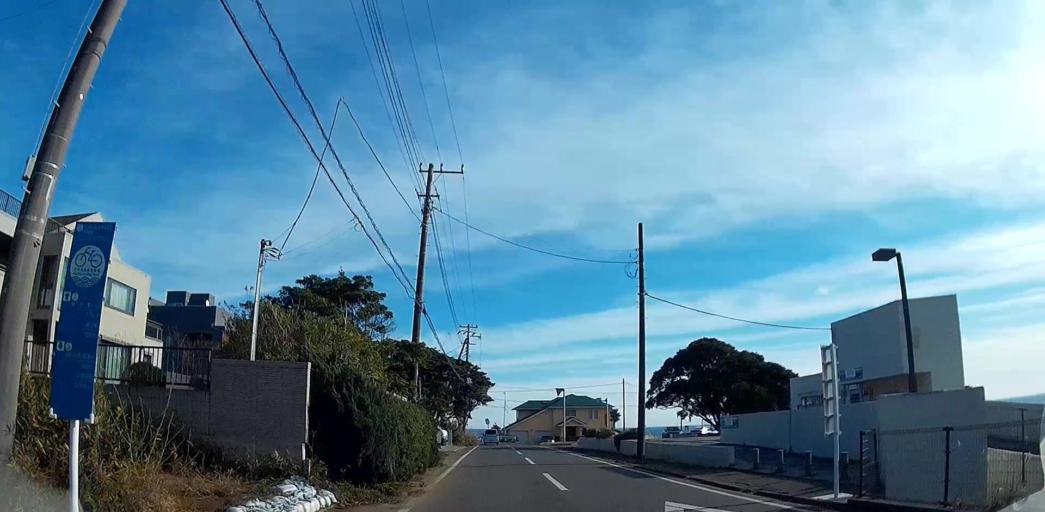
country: JP
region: Chiba
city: Hasaki
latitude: 35.7057
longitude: 140.8534
